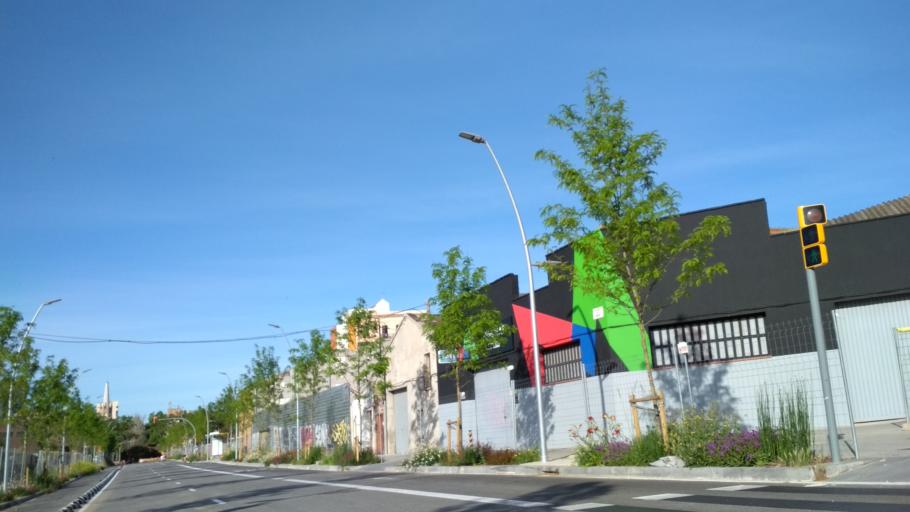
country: ES
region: Catalonia
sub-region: Provincia de Barcelona
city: Sant Marti
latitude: 41.4136
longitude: 2.2073
